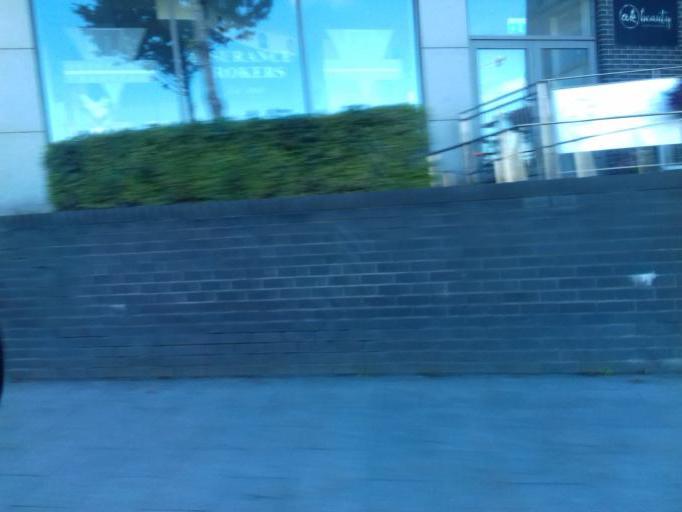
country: IE
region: Leinster
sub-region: An Mhi
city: Ashbourne
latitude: 53.5144
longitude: -6.4031
